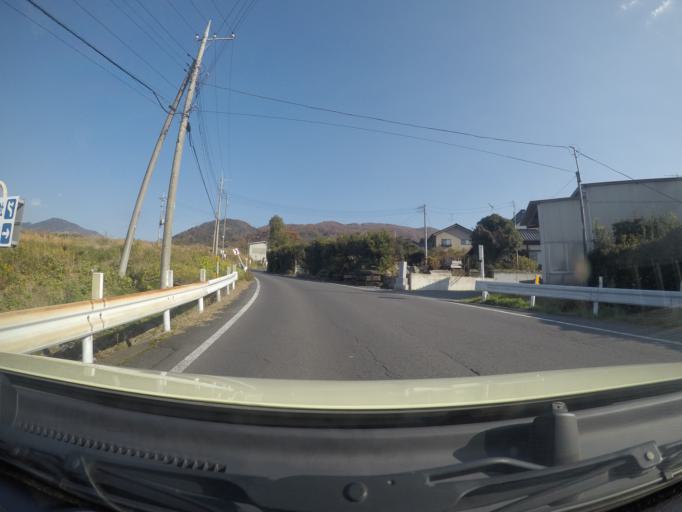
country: JP
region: Ibaraki
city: Makabe
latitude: 36.2696
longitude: 140.1125
